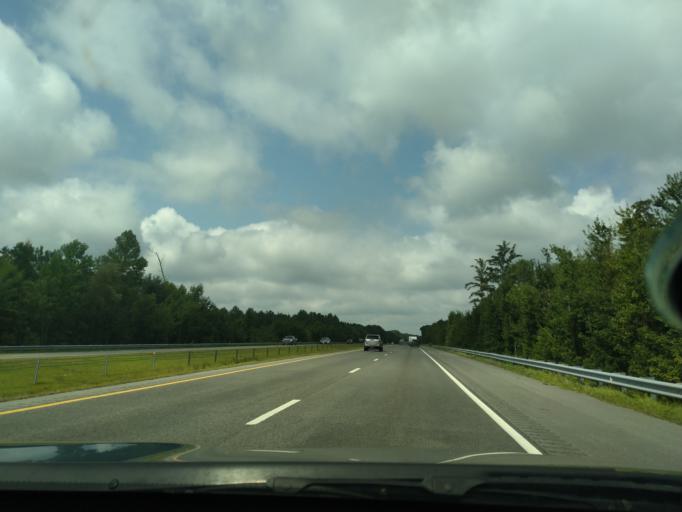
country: US
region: North Carolina
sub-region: Martin County
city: Robersonville
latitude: 35.8329
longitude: -77.2817
